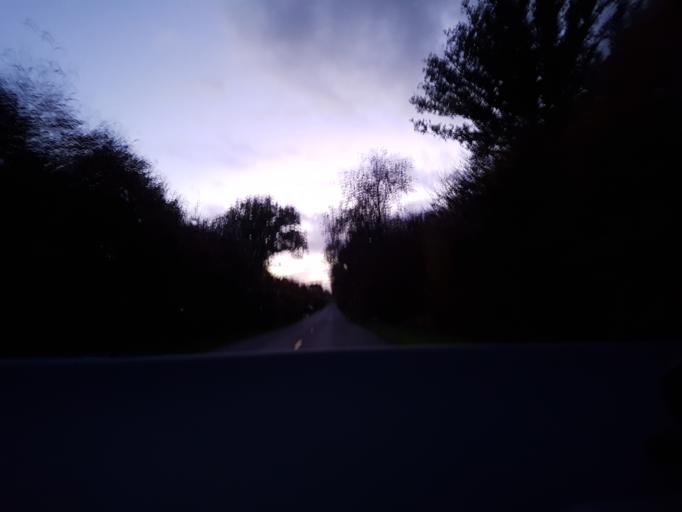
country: FR
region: Poitou-Charentes
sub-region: Departement des Deux-Sevres
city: Lezay
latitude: 46.2444
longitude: -0.0586
